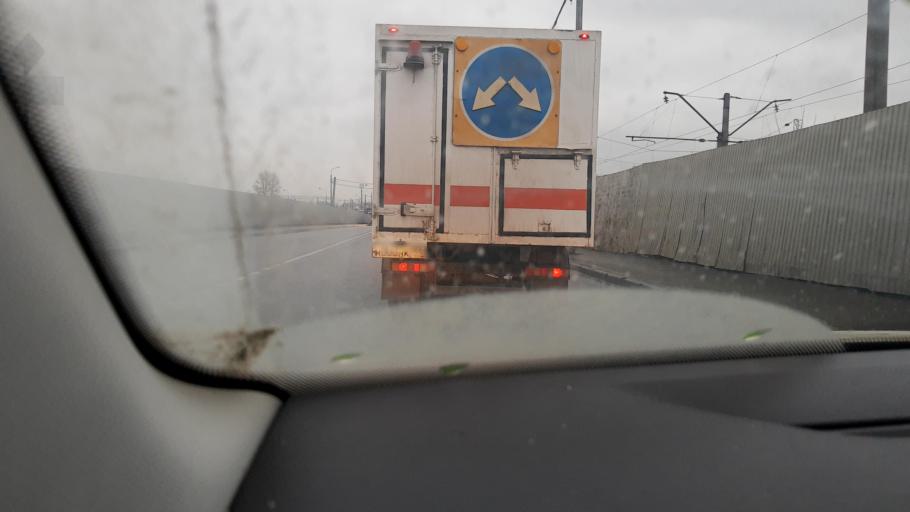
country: RU
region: Moscow
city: Mar'ino
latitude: 55.6636
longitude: 37.7149
